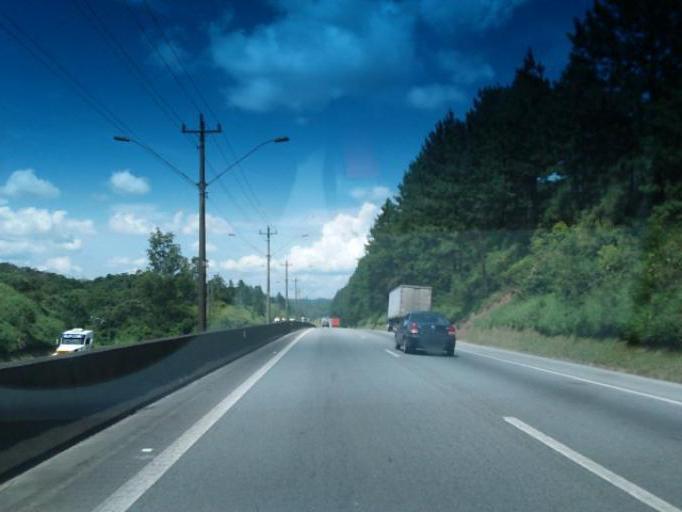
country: BR
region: Sao Paulo
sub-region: Sao Lourenco Da Serra
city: Sao Lourenco da Serra
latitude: -23.8678
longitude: -46.9542
